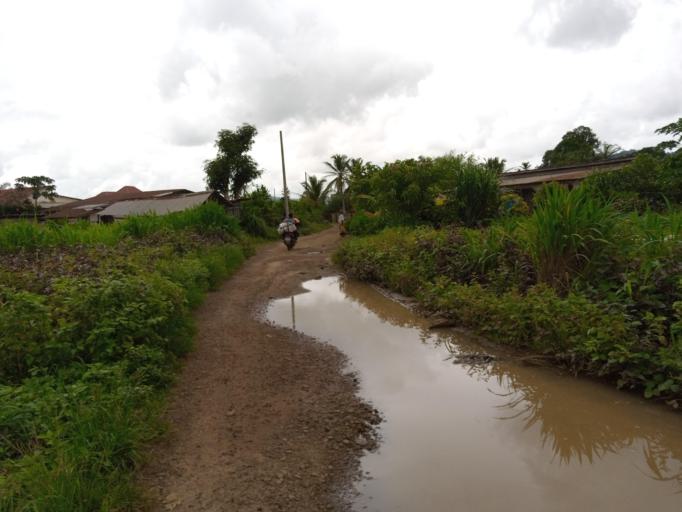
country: SL
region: Southern Province
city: Moyamba
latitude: 8.1656
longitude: -12.4254
